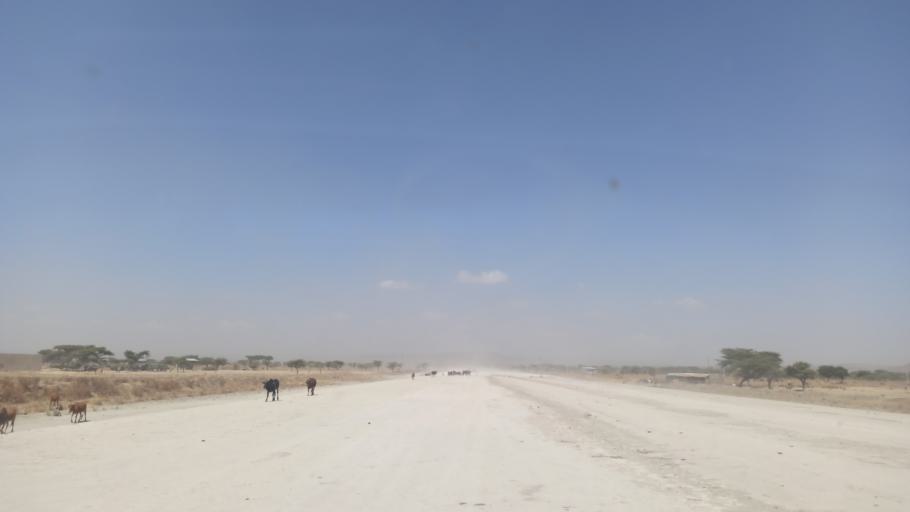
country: ET
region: Oromiya
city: Ziway
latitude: 7.7248
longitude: 38.6287
